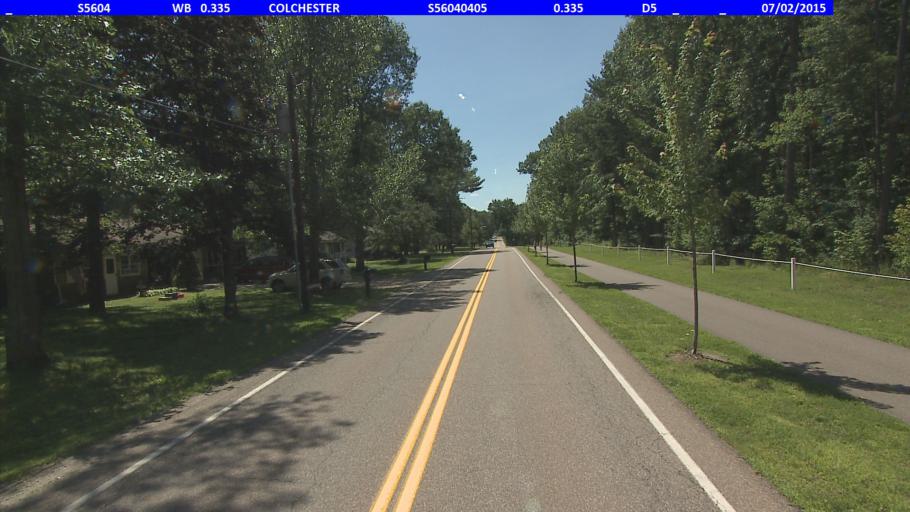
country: US
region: Vermont
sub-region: Chittenden County
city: Burlington
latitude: 44.5478
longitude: -73.2634
